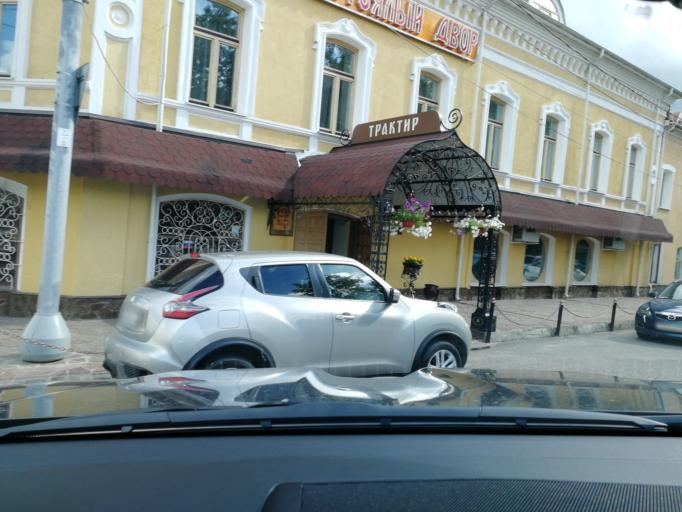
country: RU
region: Moskovskaya
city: Serpukhov
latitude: 54.9127
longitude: 37.4176
